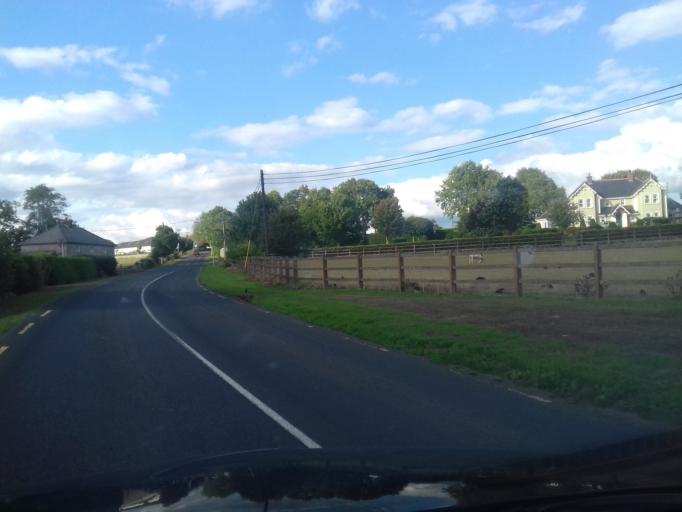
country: IE
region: Leinster
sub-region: Loch Garman
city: New Ross
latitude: 52.4500
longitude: -6.9628
